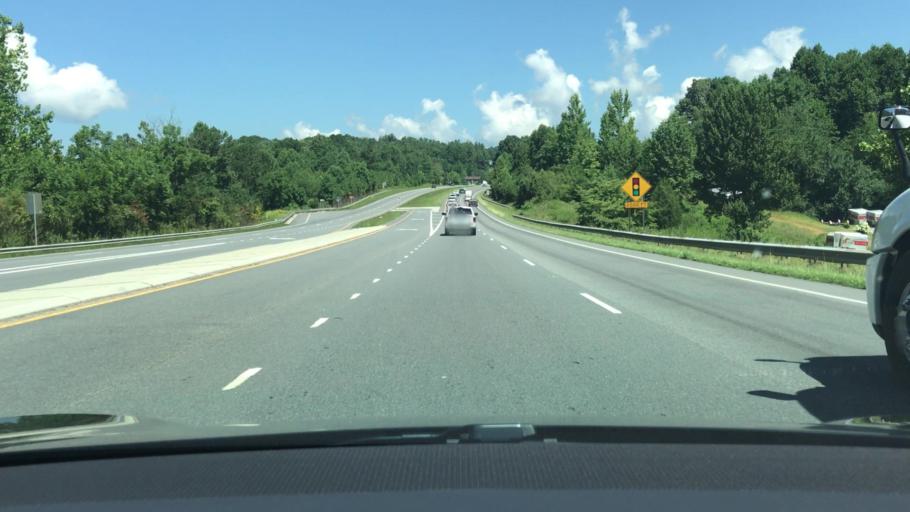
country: US
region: North Carolina
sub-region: Macon County
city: Franklin
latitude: 35.1885
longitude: -83.3597
